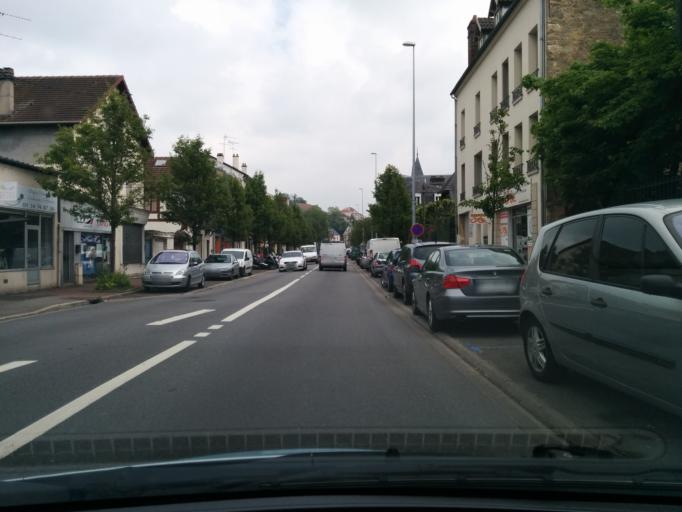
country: FR
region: Ile-de-France
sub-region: Departement des Yvelines
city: Meulan-en-Yvelines
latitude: 49.0050
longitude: 1.9016
